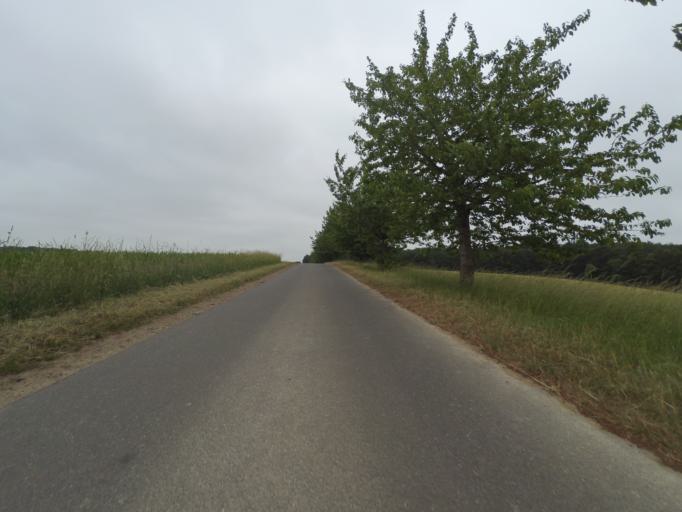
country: DE
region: Mecklenburg-Vorpommern
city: Goldberg
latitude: 53.5616
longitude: 12.0223
